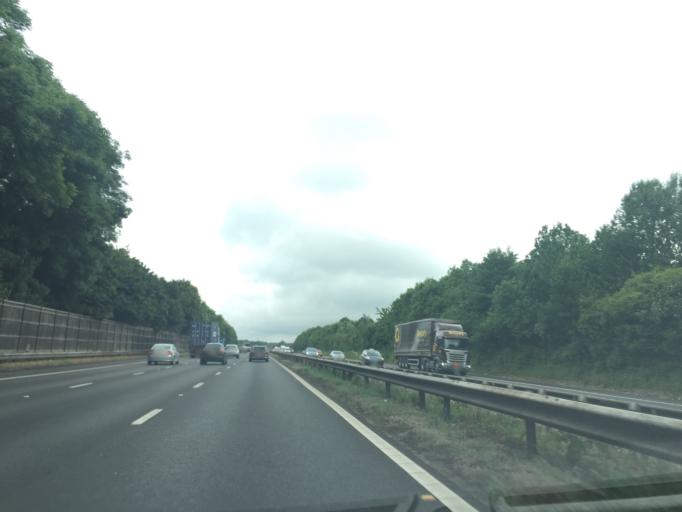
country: GB
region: England
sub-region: Hampshire
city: Eastleigh
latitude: 50.9884
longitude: -1.3621
